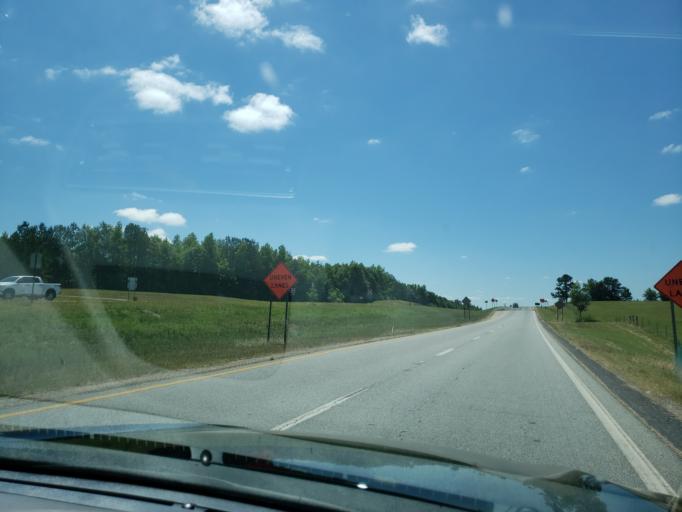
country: US
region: Alabama
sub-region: Lee County
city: Auburn
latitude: 32.6868
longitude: -85.4964
